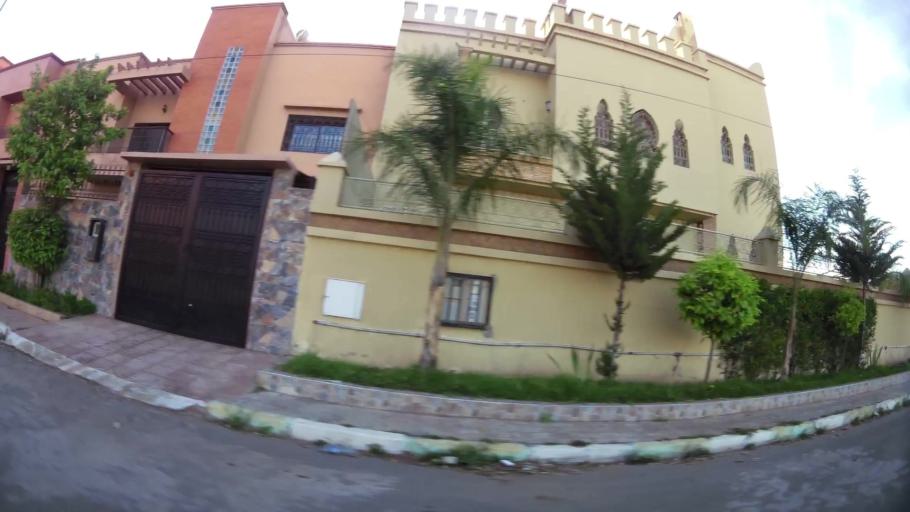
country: MA
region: Marrakech-Tensift-Al Haouz
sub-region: Marrakech
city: Marrakesh
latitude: 31.6812
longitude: -8.0640
